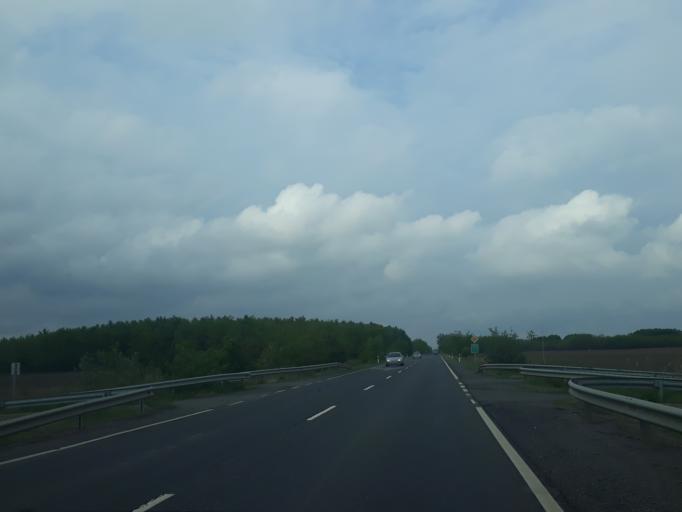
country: HU
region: Szabolcs-Szatmar-Bereg
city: Ajak
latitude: 48.1661
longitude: 22.0328
